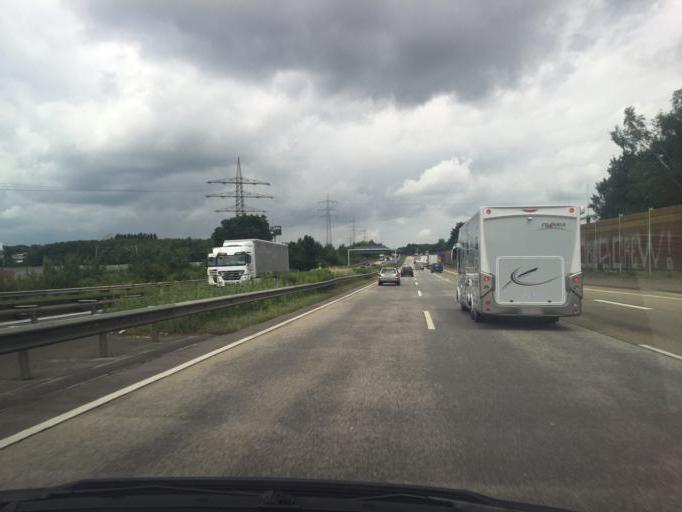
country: DE
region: Rheinland-Pfalz
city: Ebernhahn
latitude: 50.4694
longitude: 7.7627
